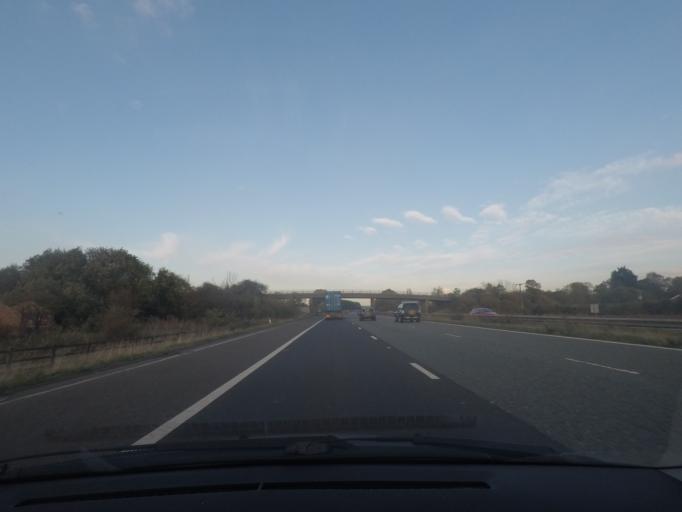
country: GB
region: England
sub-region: North Lincolnshire
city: Brigg
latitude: 53.5706
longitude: -0.4733
